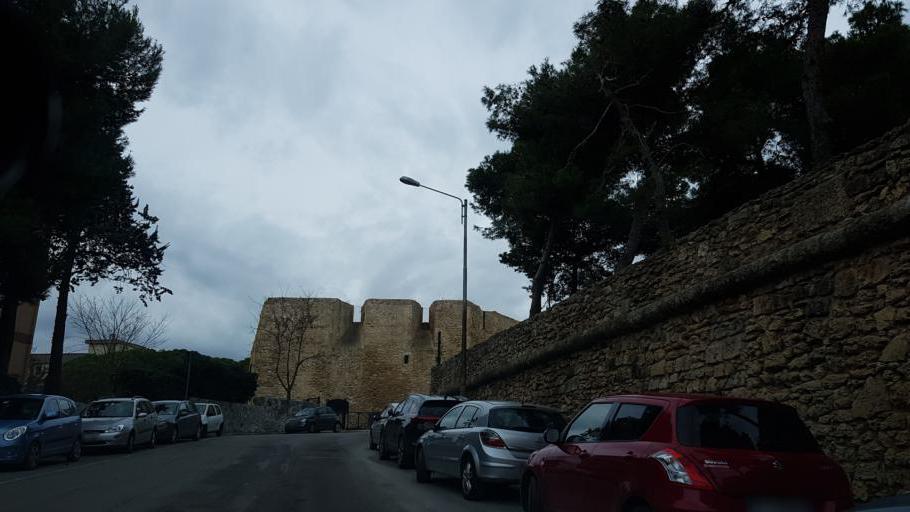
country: IT
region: Apulia
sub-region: Provincia di Brindisi
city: Brindisi
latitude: 40.6322
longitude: 17.9432
